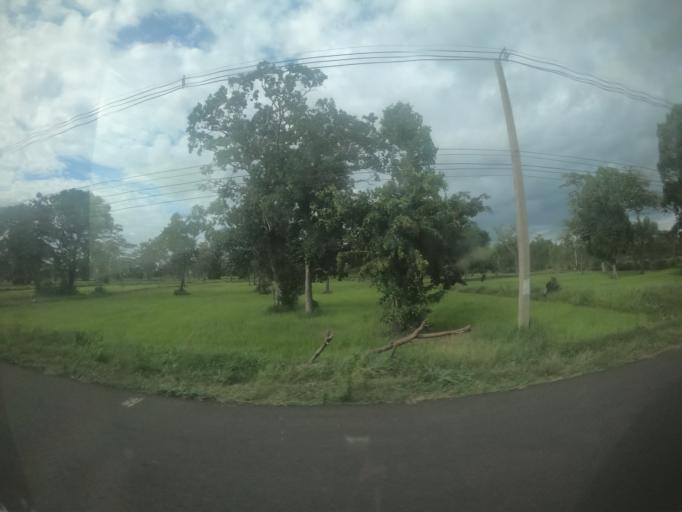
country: TH
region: Surin
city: Prasat
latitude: 14.5731
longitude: 103.4853
